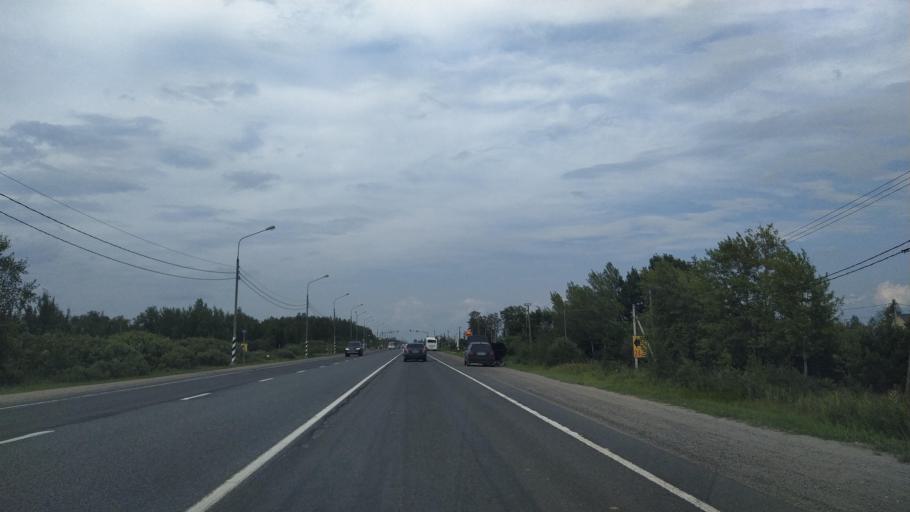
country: RU
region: Novgorod
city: Pankovka
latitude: 58.4765
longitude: 31.1781
